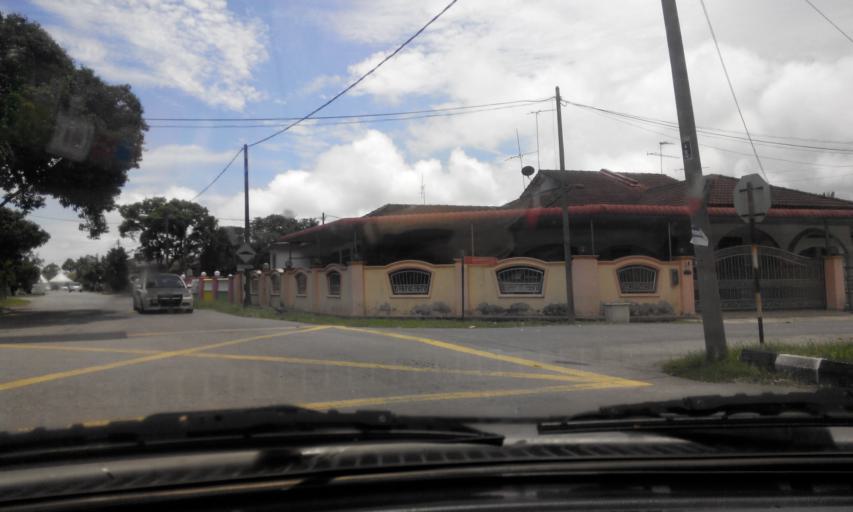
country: MY
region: Perak
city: Parit Buntar
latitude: 5.1228
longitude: 100.4861
